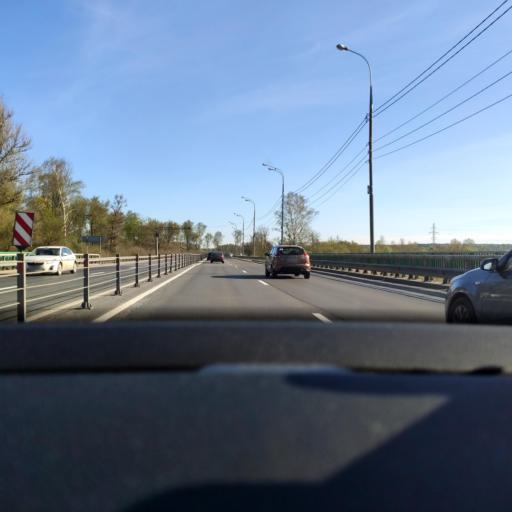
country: RU
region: Moskovskaya
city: Yakhroma
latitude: 56.2735
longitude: 37.5026
